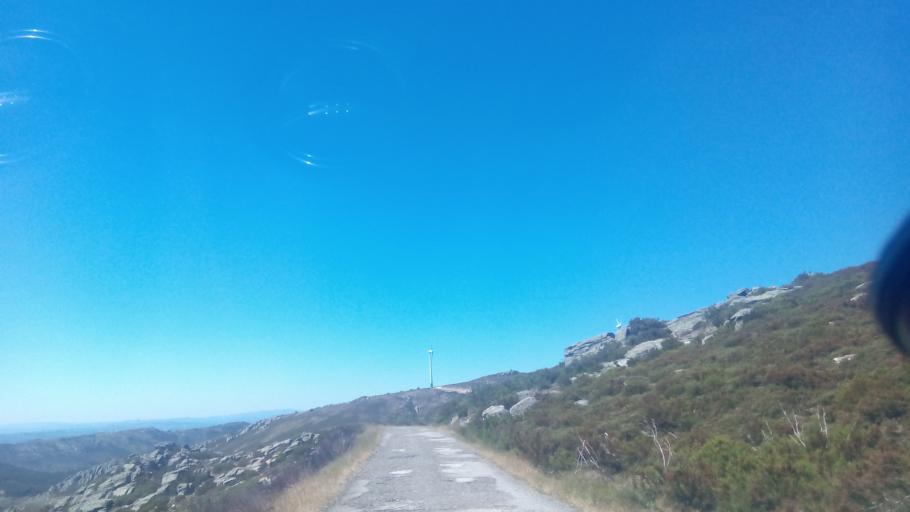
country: PT
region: Vila Real
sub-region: Mesao Frio
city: Mesao Frio
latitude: 41.2579
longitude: -7.8972
